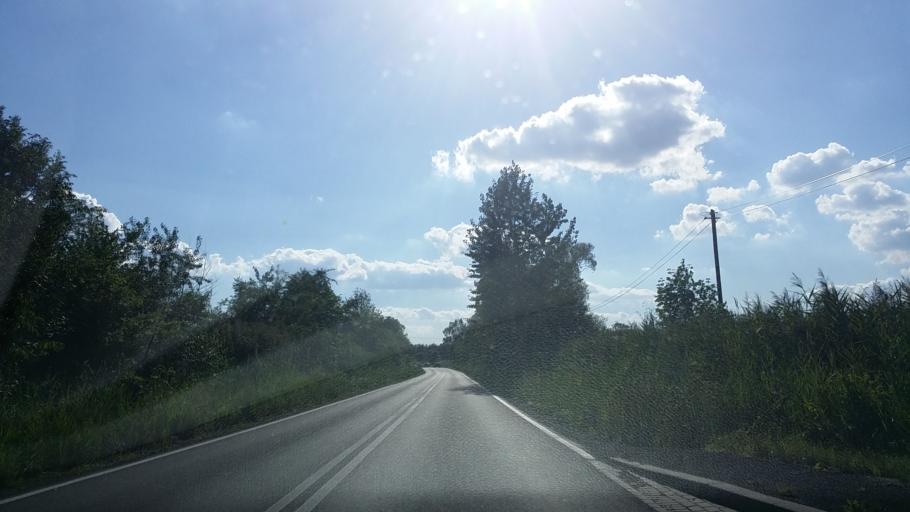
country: PL
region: Lesser Poland Voivodeship
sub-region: Powiat wadowicki
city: Tomice
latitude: 49.9099
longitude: 19.4966
